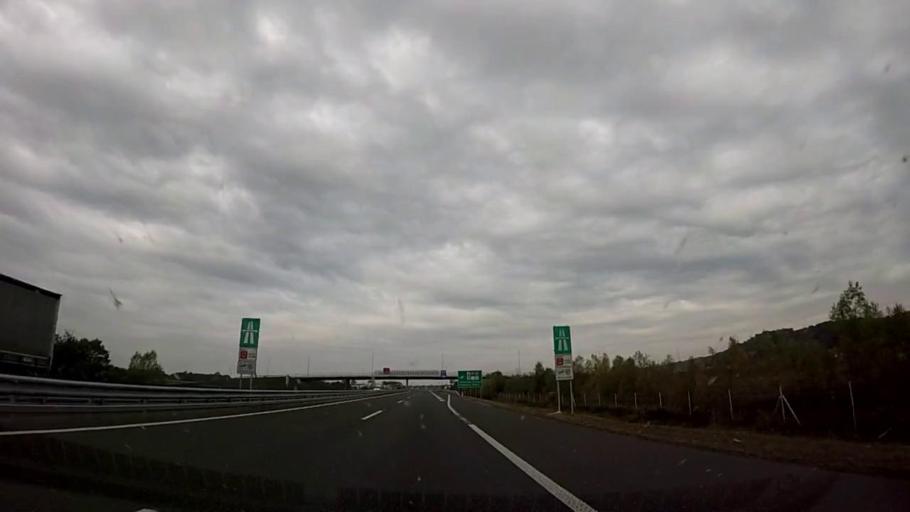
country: HR
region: Medimurska
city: Peklenica
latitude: 46.5204
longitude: 16.5234
